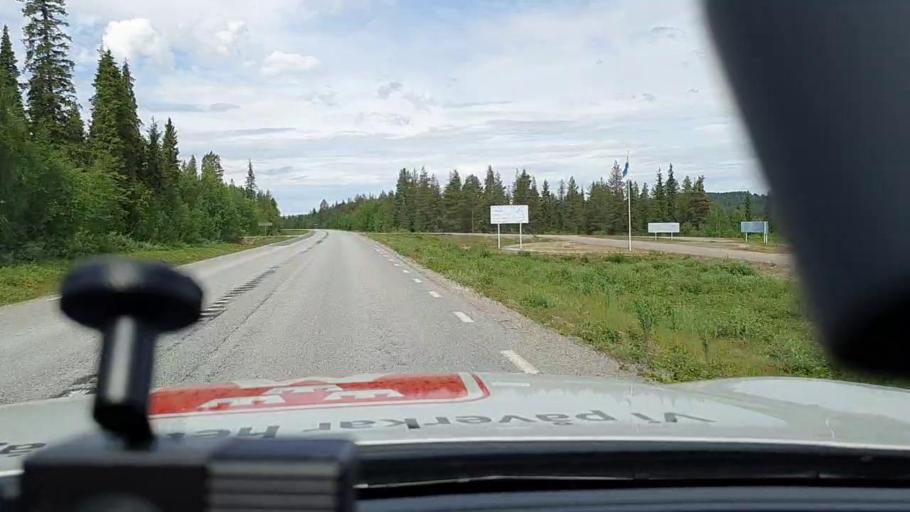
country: SE
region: Norrbotten
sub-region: Jokkmokks Kommun
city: Jokkmokk
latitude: 66.5529
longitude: 20.1150
